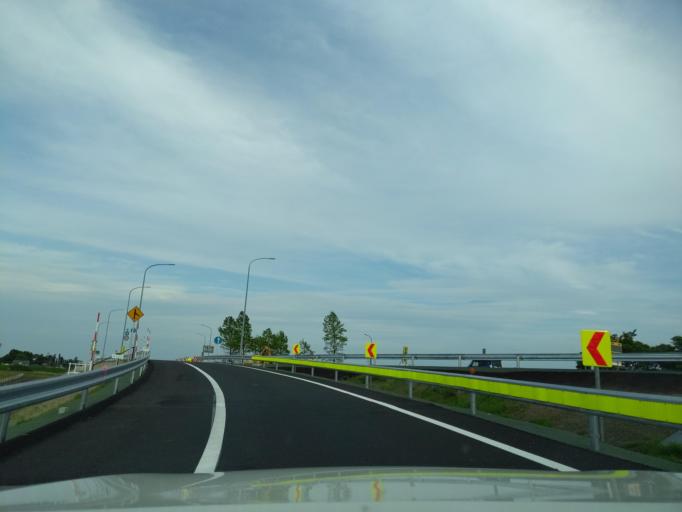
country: JP
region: Miyagi
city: Sendai
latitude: 38.2136
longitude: 140.9051
